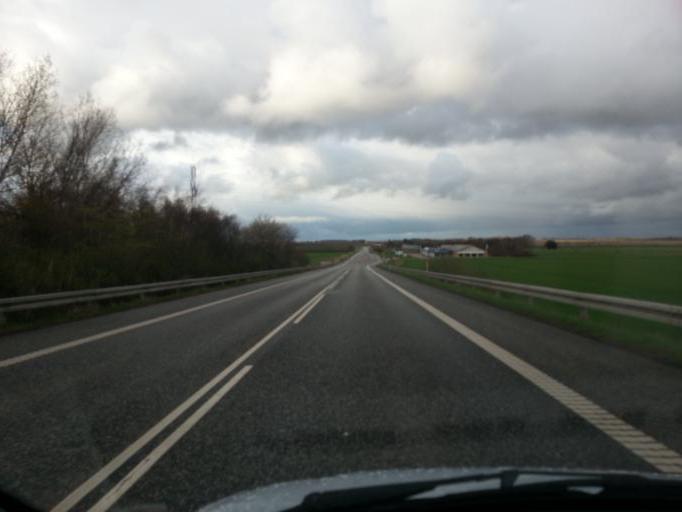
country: DK
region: Central Jutland
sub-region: Holstebro Kommune
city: Ulfborg
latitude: 56.2806
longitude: 8.3283
